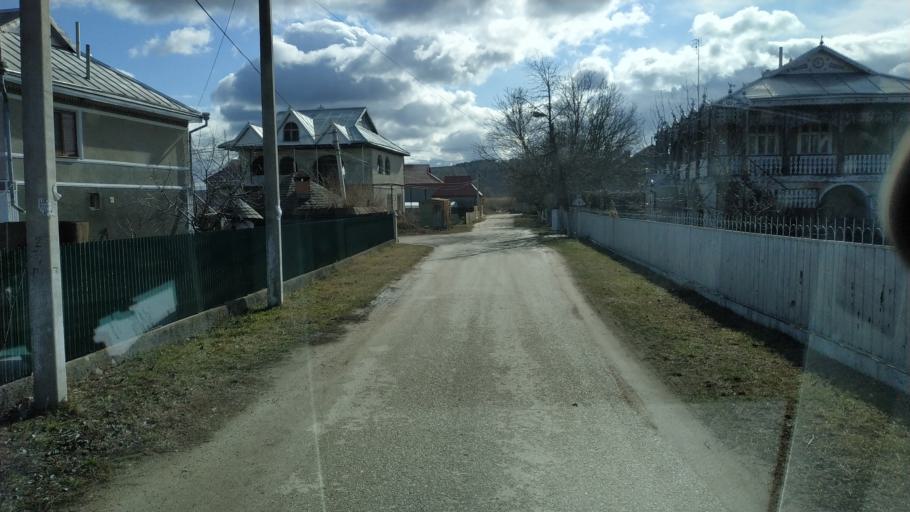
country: MD
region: Stinga Nistrului
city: Bucovat
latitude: 47.1851
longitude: 28.4708
